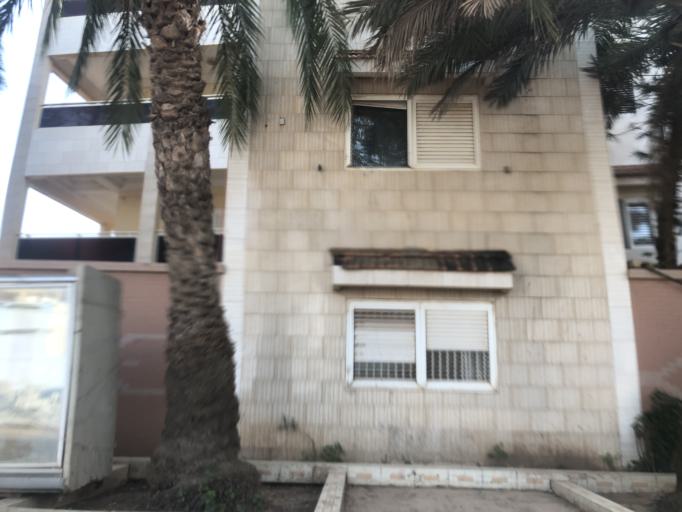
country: SN
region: Dakar
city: Mermoz Boabab
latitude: 14.7330
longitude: -17.4958
